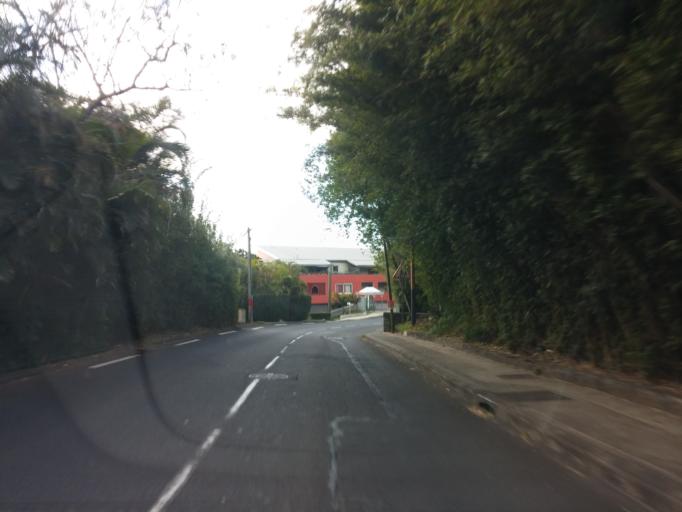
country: RE
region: Reunion
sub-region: Reunion
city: Saint-Denis
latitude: -20.8903
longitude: 55.4225
